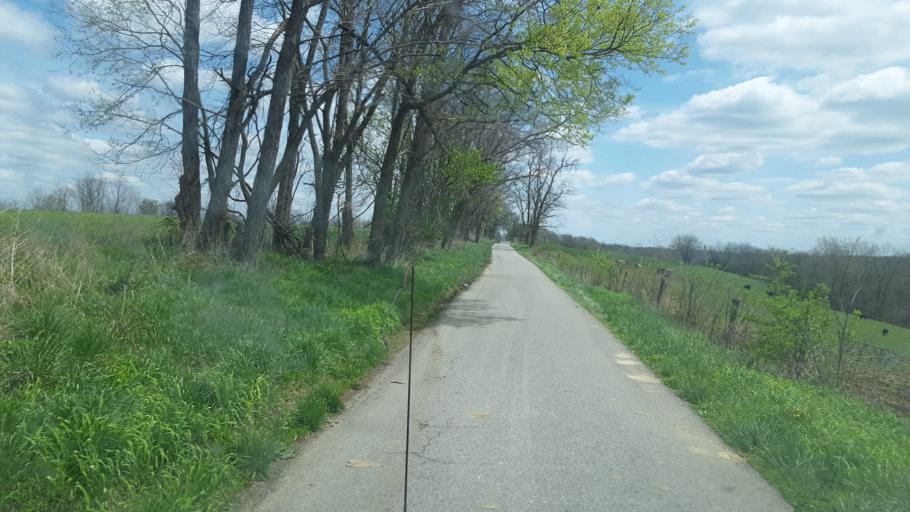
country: US
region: Kentucky
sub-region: Owen County
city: Owenton
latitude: 38.6742
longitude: -84.8102
